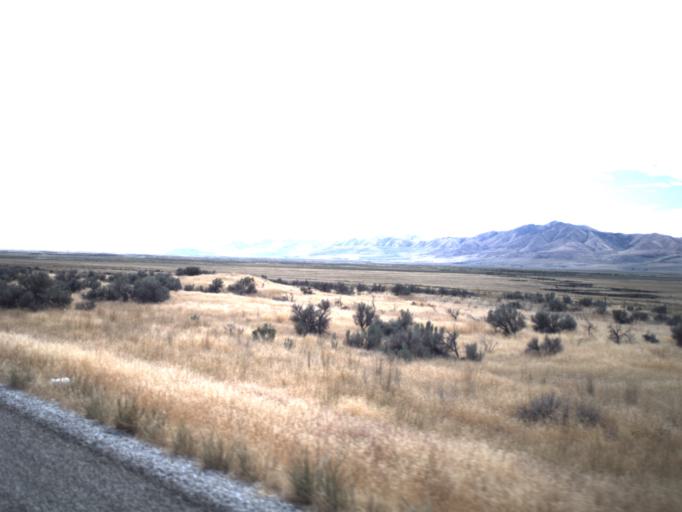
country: US
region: Utah
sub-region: Box Elder County
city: Tremonton
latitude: 41.6536
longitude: -112.4390
